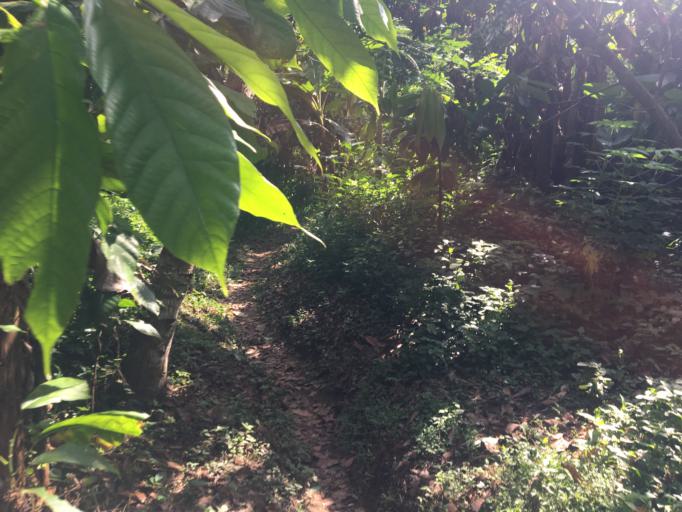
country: TG
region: Plateaux
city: Kpalime
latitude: 6.9504
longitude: 0.6331
